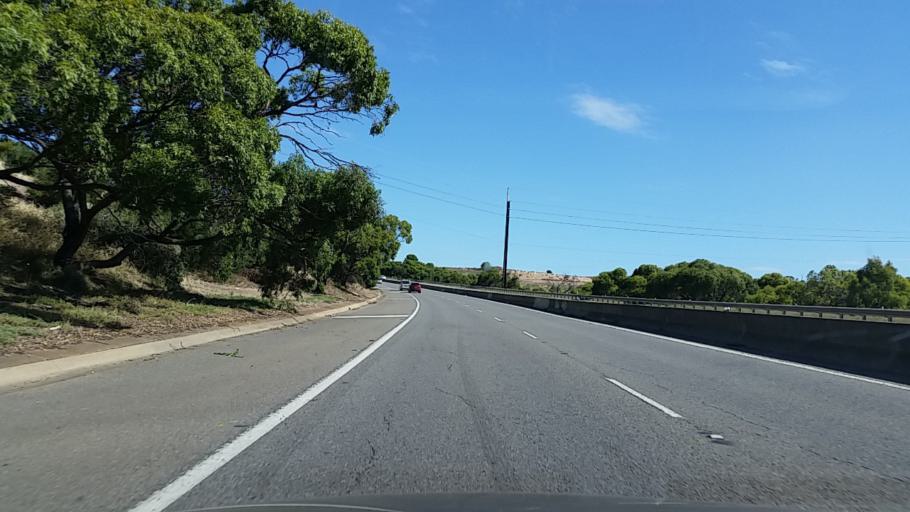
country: AU
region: South Australia
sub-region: Onkaparinga
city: Reynella
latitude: -35.0920
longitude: 138.4963
